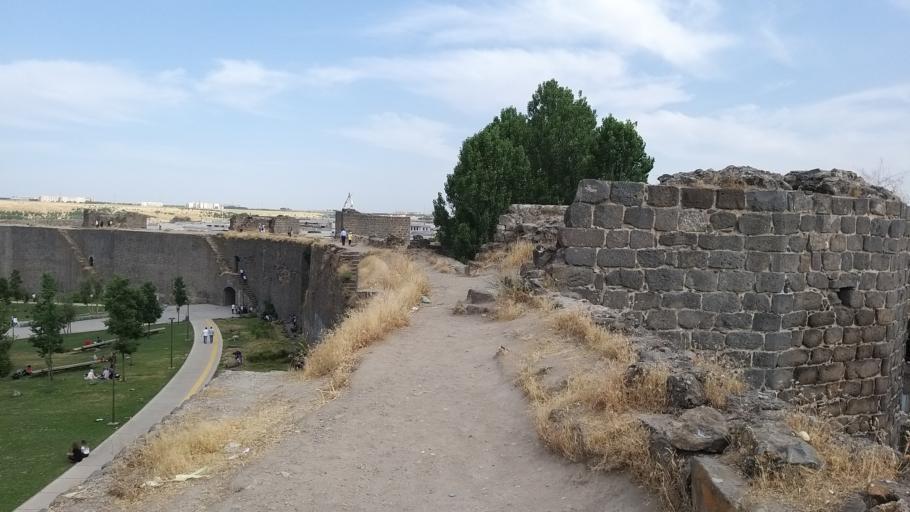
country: TR
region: Diyarbakir
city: Sur
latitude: 37.9143
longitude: 40.2409
